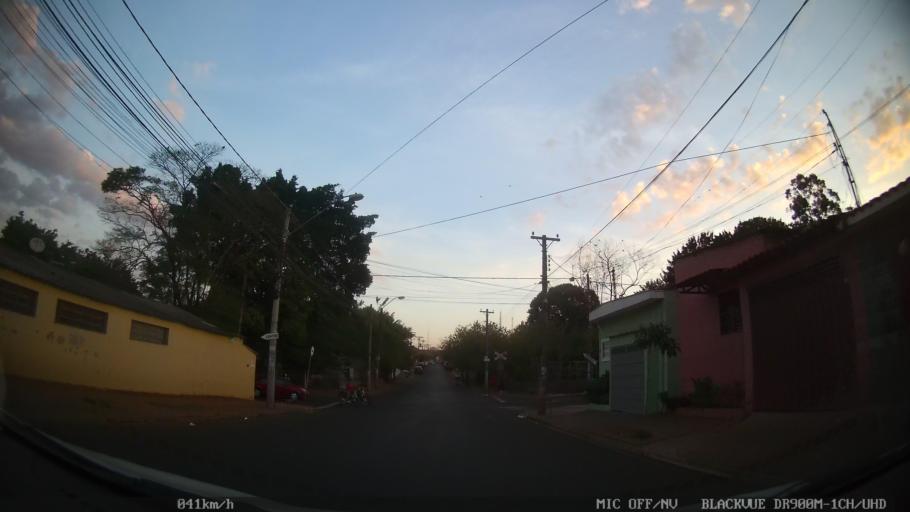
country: BR
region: Sao Paulo
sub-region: Ribeirao Preto
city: Ribeirao Preto
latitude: -21.1471
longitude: -47.8233
